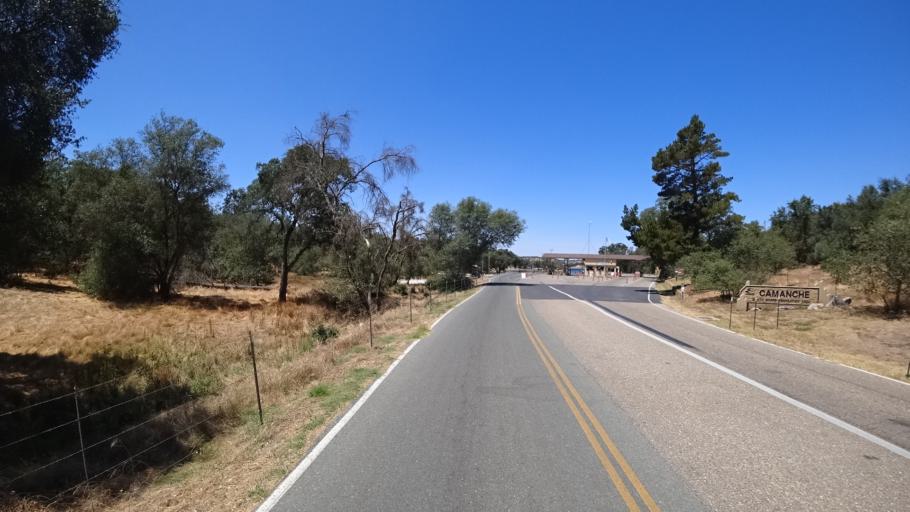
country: US
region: California
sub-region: Calaveras County
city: Valley Springs
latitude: 38.2111
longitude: -120.9166
